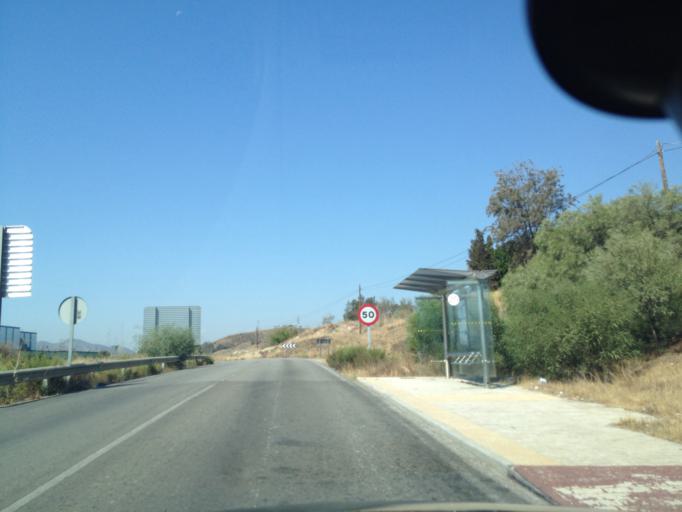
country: ES
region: Andalusia
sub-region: Provincia de Malaga
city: Alhaurin de la Torre
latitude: 36.7197
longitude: -4.5154
